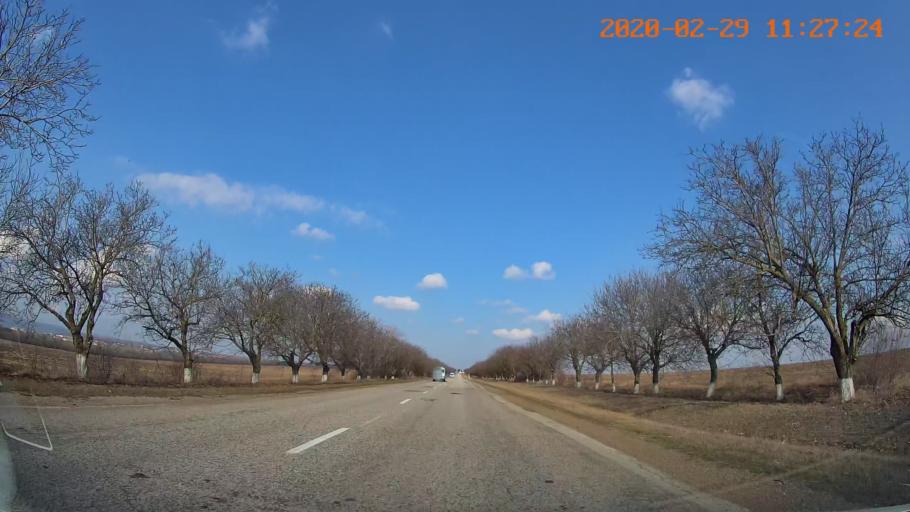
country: MD
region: Telenesti
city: Cocieri
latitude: 47.4676
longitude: 29.1427
